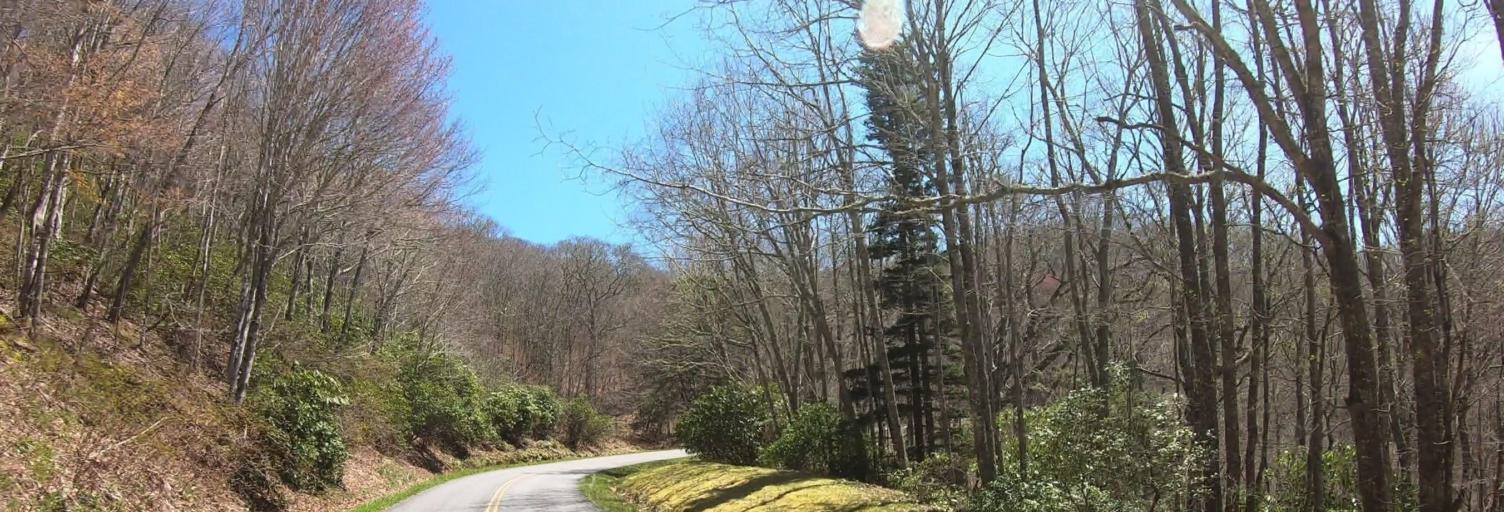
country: US
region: North Carolina
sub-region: Haywood County
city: Maggie Valley
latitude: 35.4804
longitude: -83.1494
